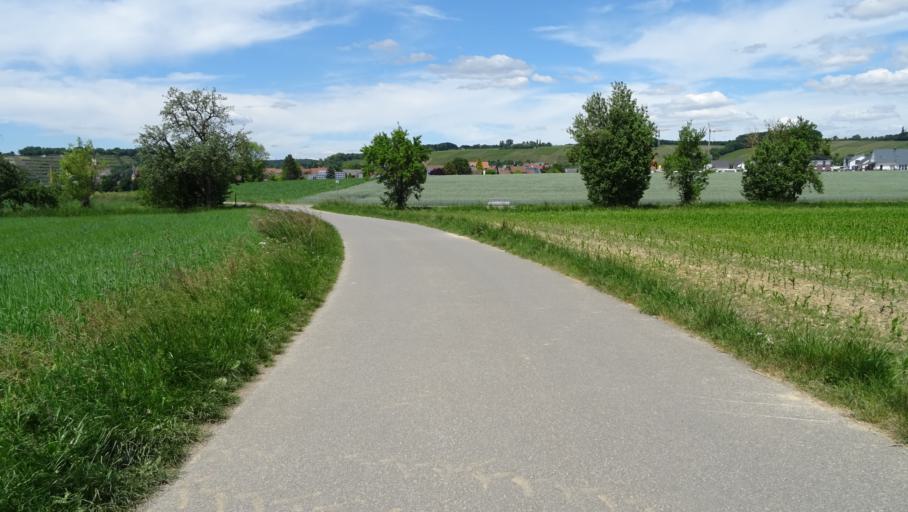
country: DE
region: Baden-Wuerttemberg
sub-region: Regierungsbezirk Stuttgart
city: Gundelsheim
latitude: 49.2741
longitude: 9.1648
